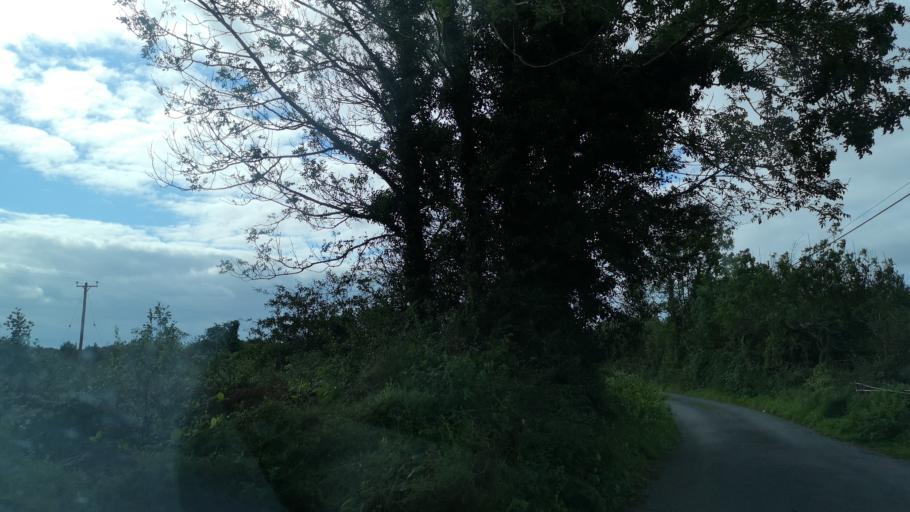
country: IE
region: Connaught
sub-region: County Galway
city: Moycullen
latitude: 53.3205
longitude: -9.1432
